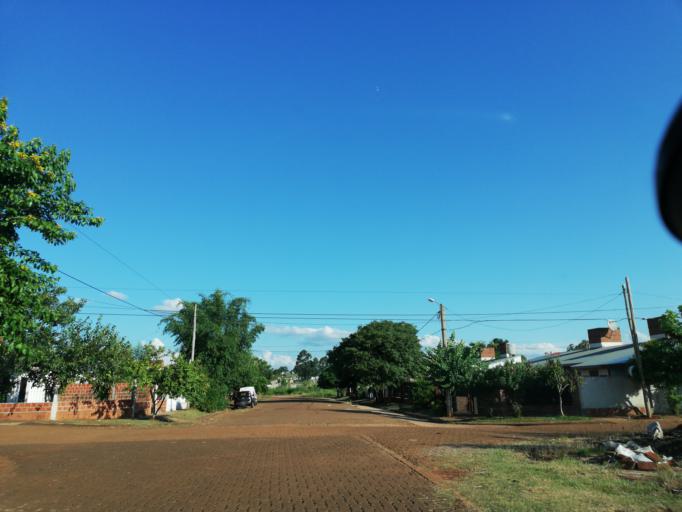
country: AR
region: Misiones
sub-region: Departamento de Capital
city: Posadas
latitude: -27.4313
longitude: -55.9491
